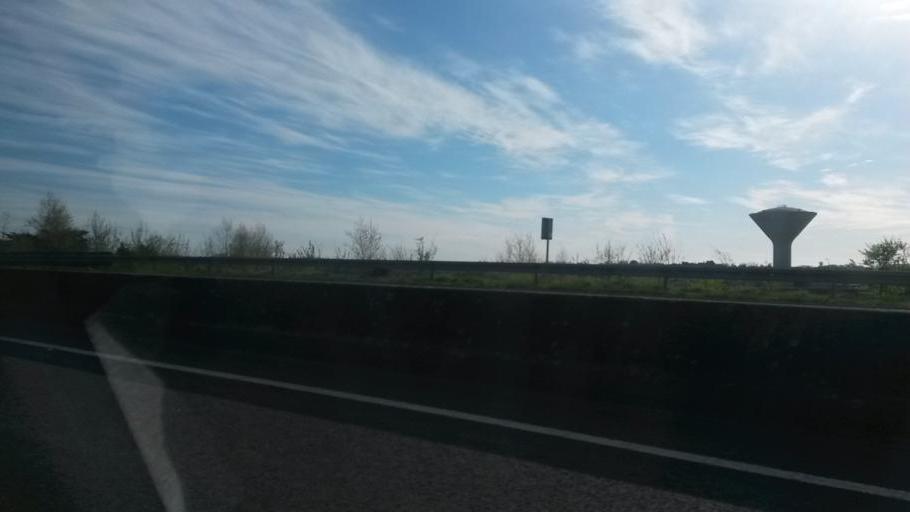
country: IE
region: Leinster
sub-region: An Mhi
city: Dunshaughlin
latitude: 53.5229
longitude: -6.5571
